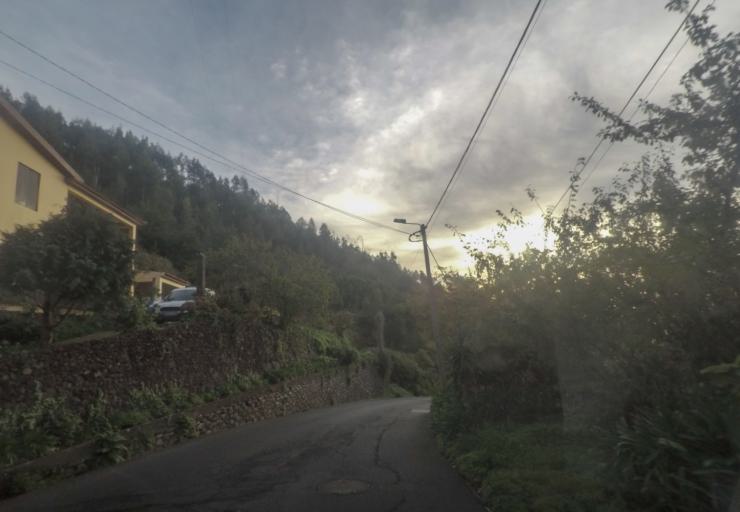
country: PT
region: Madeira
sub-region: Funchal
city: Nossa Senhora do Monte
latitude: 32.6593
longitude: -16.8730
